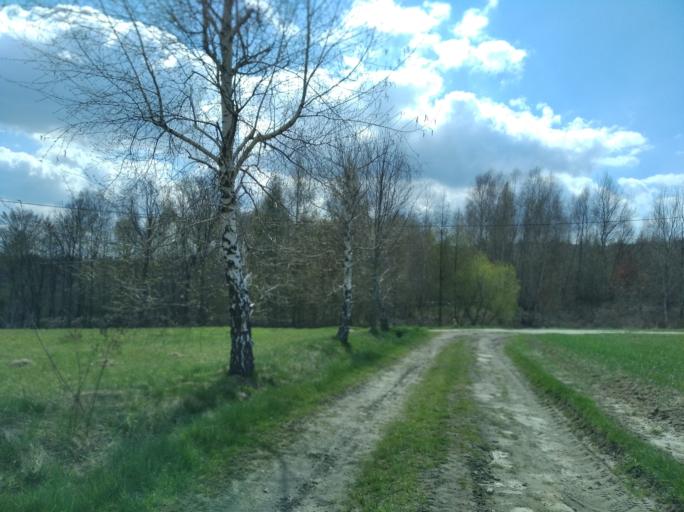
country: PL
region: Subcarpathian Voivodeship
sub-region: Powiat strzyzowski
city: Strzyzow
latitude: 49.8393
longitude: 21.7810
